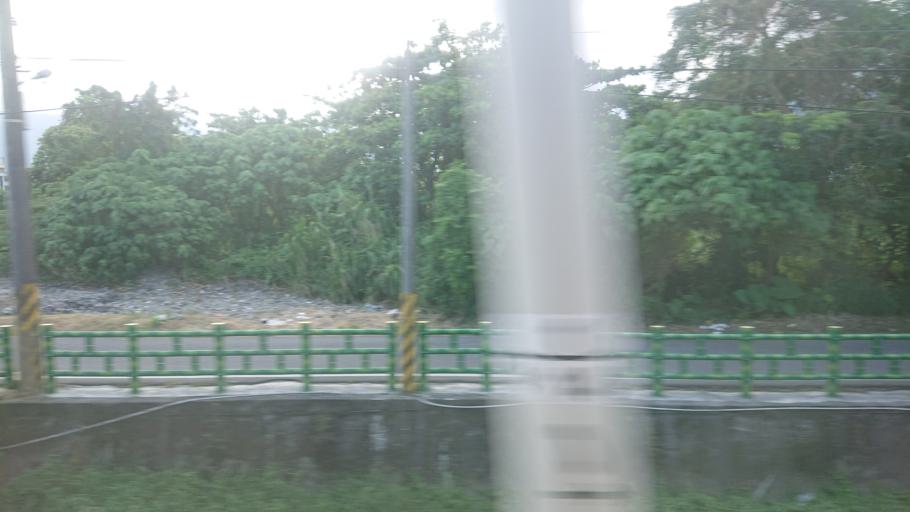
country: TW
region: Taiwan
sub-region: Hualien
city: Hualian
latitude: 23.9821
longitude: 121.5956
